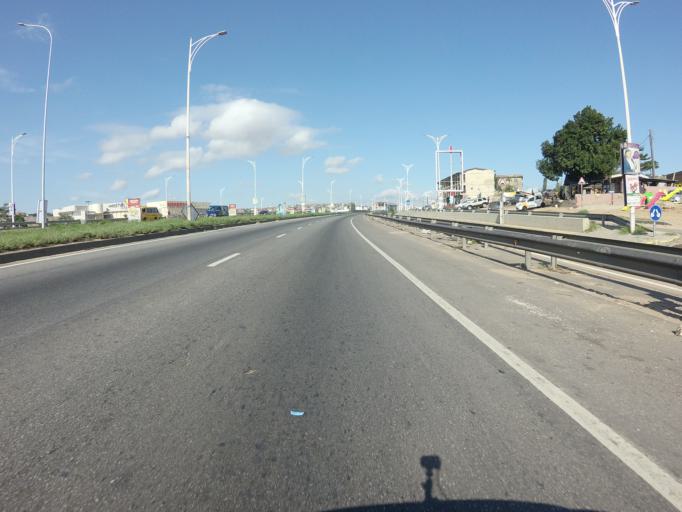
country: GH
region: Greater Accra
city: Gbawe
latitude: 5.5463
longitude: -0.3429
